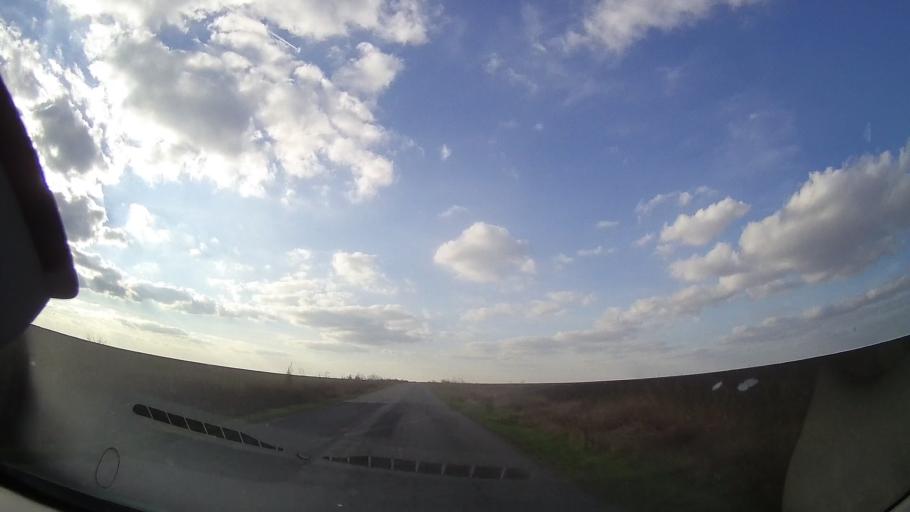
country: RO
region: Constanta
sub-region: Comuna Negru Voda
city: Negru Voda
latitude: 43.8223
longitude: 28.1564
